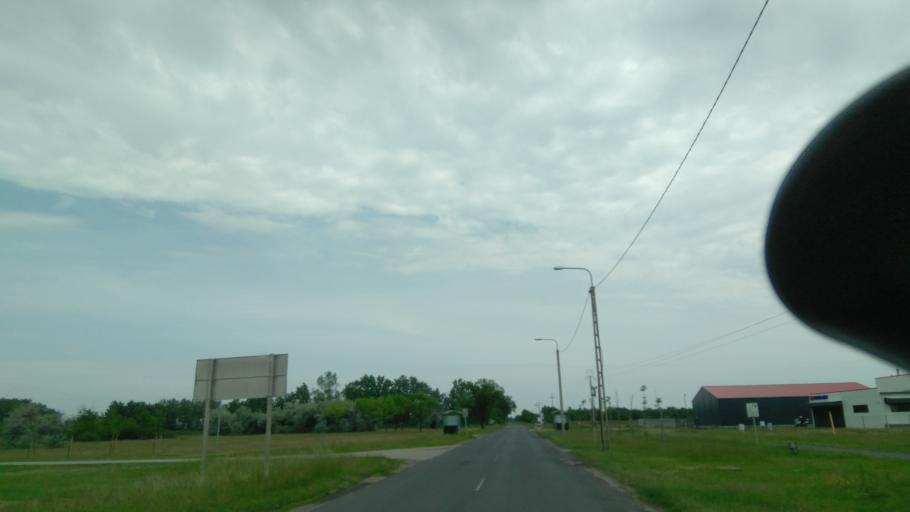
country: HU
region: Bekes
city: Szeghalom
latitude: 47.0350
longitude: 21.1813
